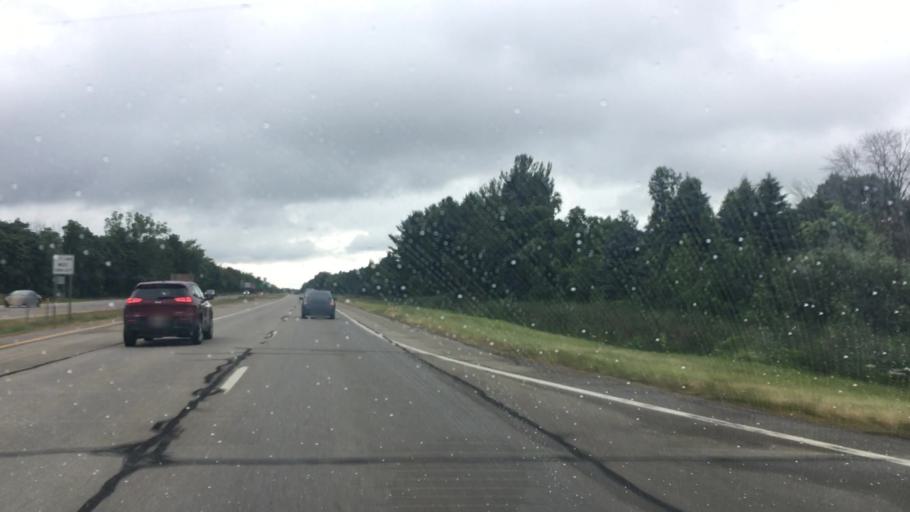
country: US
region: Michigan
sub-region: Ottawa County
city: Beechwood
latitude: 42.8924
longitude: -86.1283
